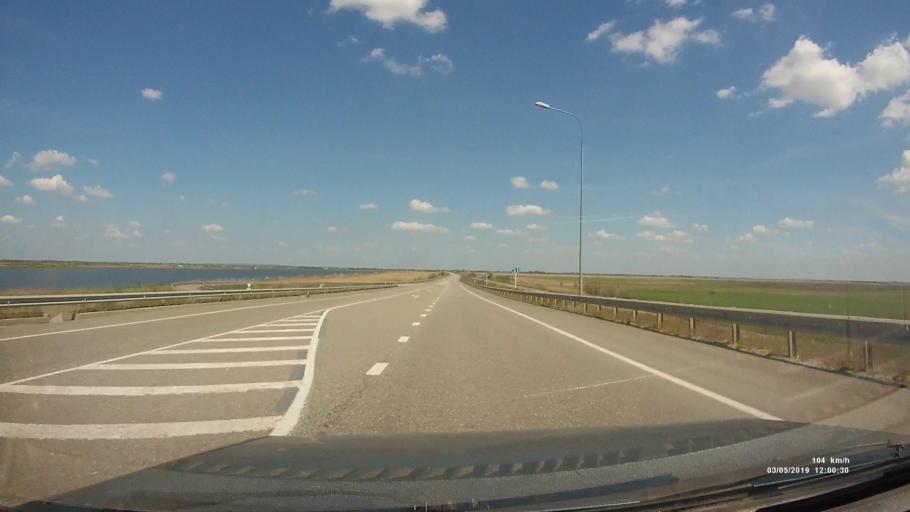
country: RU
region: Rostov
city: Bagayevskaya
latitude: 47.2499
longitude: 40.3409
